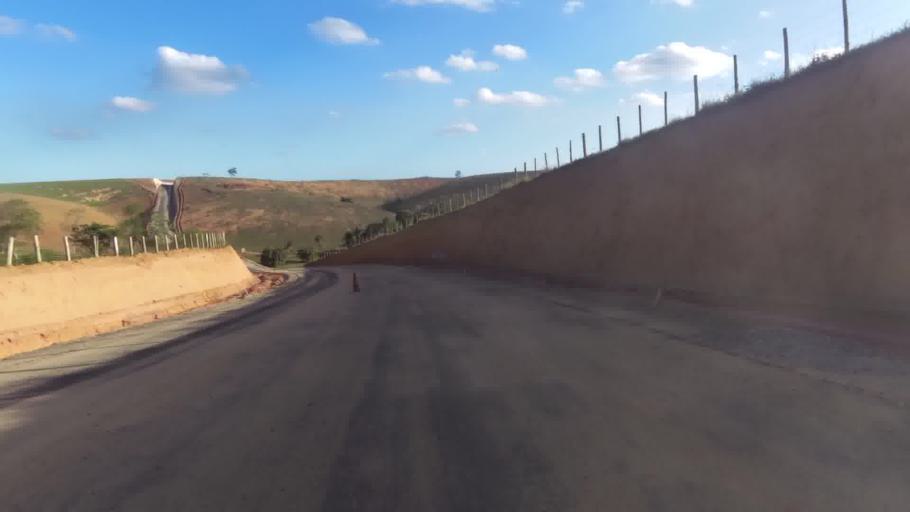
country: BR
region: Espirito Santo
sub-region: Marataizes
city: Marataizes
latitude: -21.1120
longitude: -41.0478
